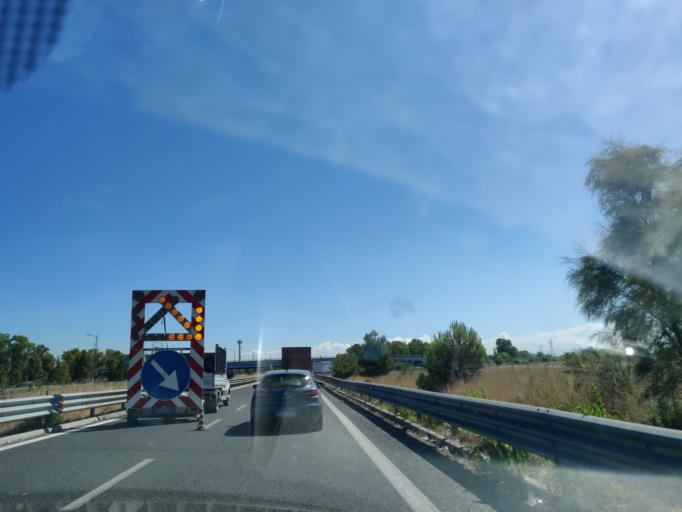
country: IT
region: Latium
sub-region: Citta metropolitana di Roma Capitale
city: Npp 23 (Parco Leonardo)
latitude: 41.8079
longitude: 12.3069
